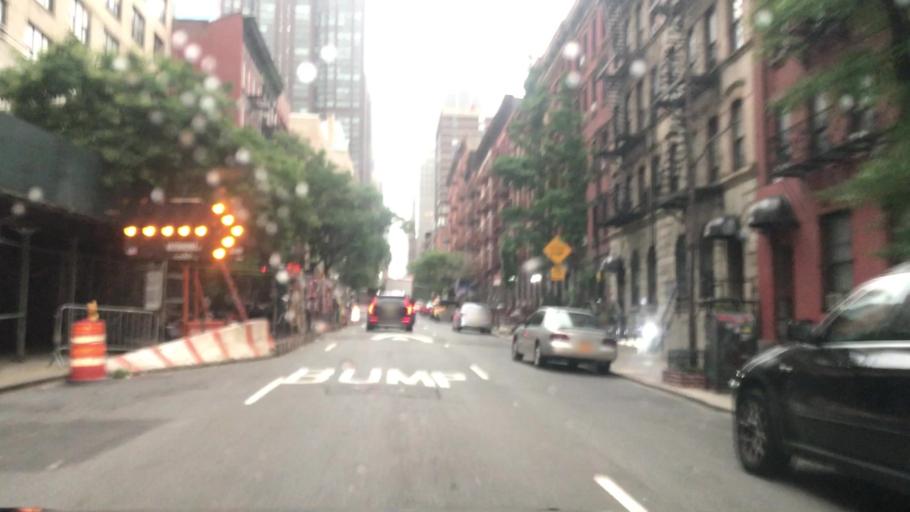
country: US
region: New York
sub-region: New York County
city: Manhattan
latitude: 40.7679
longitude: -73.9880
